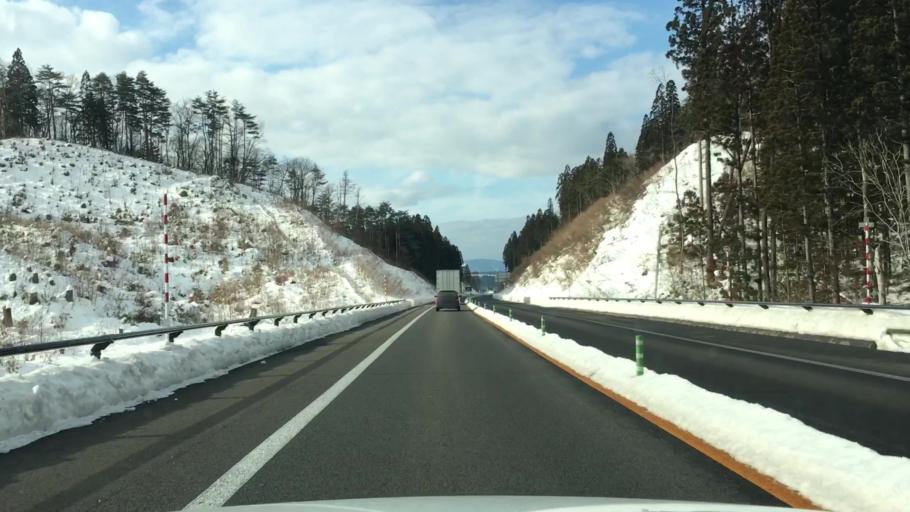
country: JP
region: Akita
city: Takanosu
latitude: 40.2101
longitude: 140.4138
